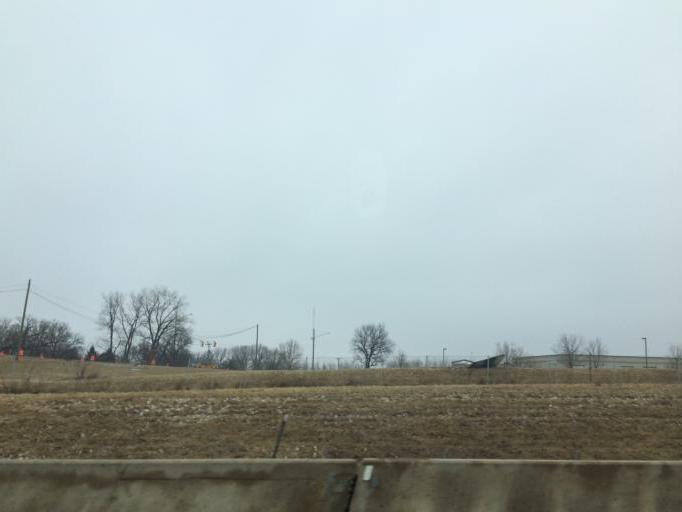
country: US
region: Illinois
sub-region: Kane County
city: Gilberts
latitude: 42.1003
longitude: -88.3796
